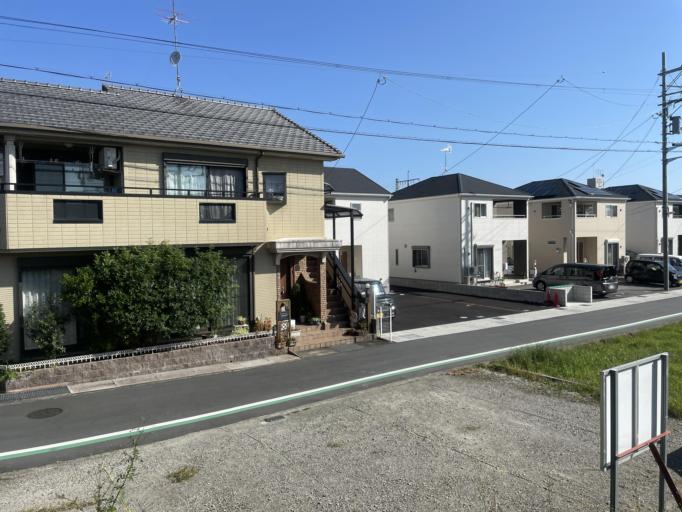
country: JP
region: Nara
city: Gose
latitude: 34.5083
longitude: 135.7246
